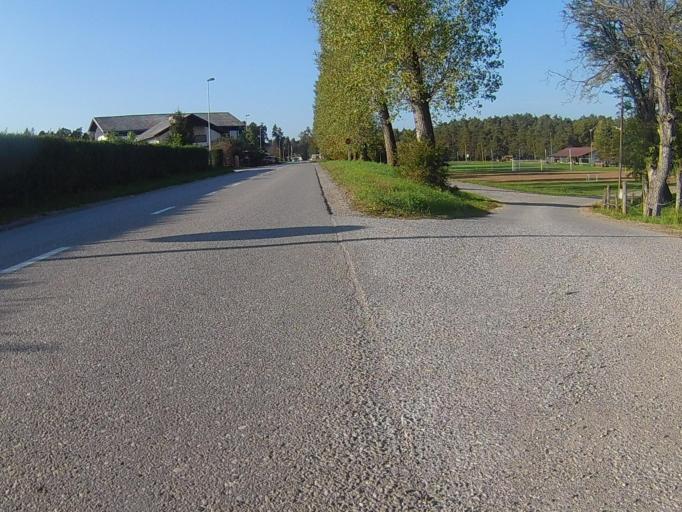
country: SI
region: Starse
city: Starse
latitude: 46.4545
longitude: 15.7312
